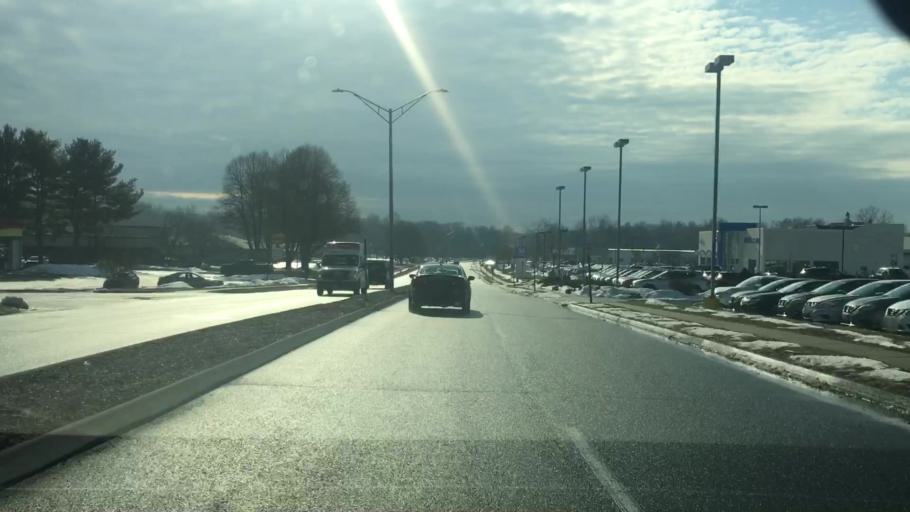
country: US
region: Connecticut
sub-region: Hartford County
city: Sherwood Manor
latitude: 41.9983
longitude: -72.5744
